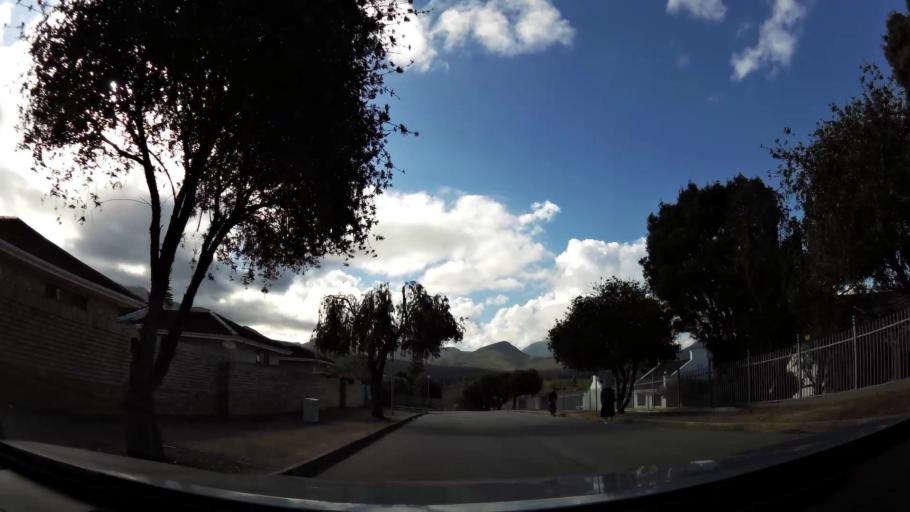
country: ZA
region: Western Cape
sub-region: Eden District Municipality
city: George
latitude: -33.9595
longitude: 22.4896
